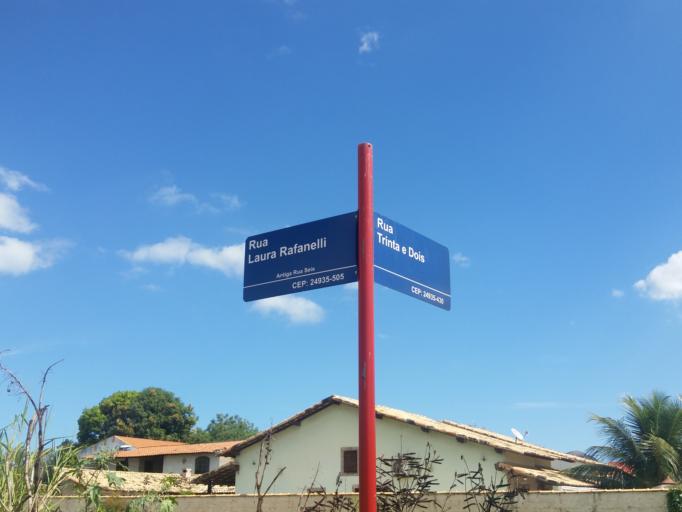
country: BR
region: Rio de Janeiro
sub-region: Marica
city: Marica
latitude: -22.9596
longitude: -42.9667
